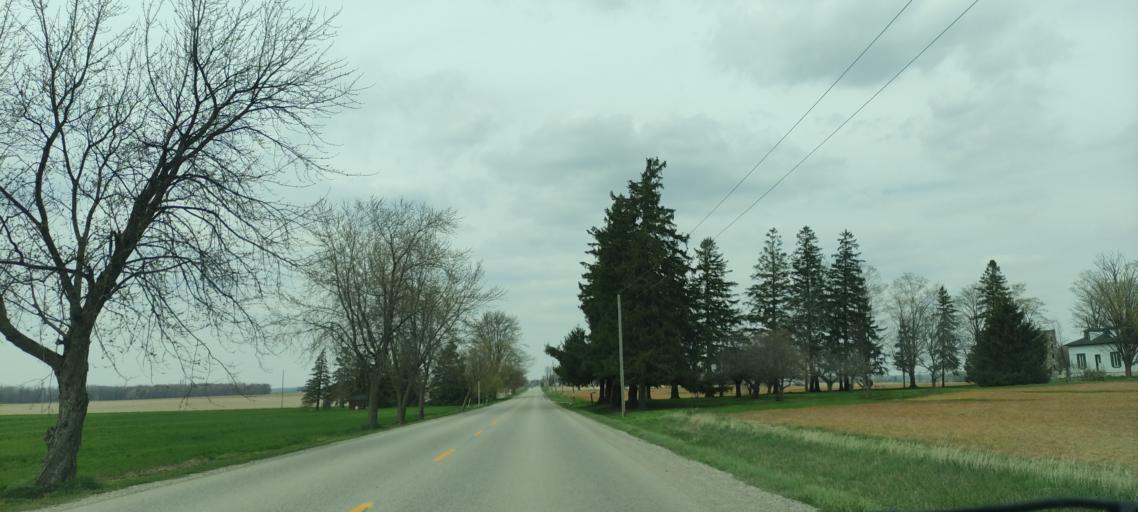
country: CA
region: Ontario
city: Stratford
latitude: 43.3130
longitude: -80.7813
